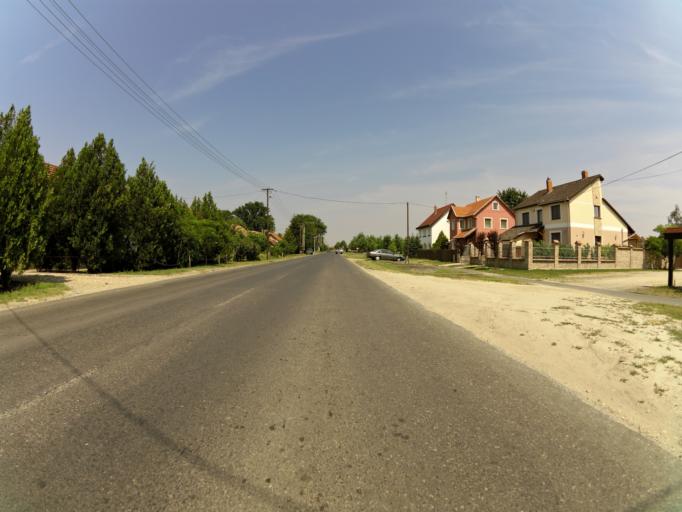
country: HU
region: Csongrad
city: Sandorfalva
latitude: 46.3646
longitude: 20.1015
